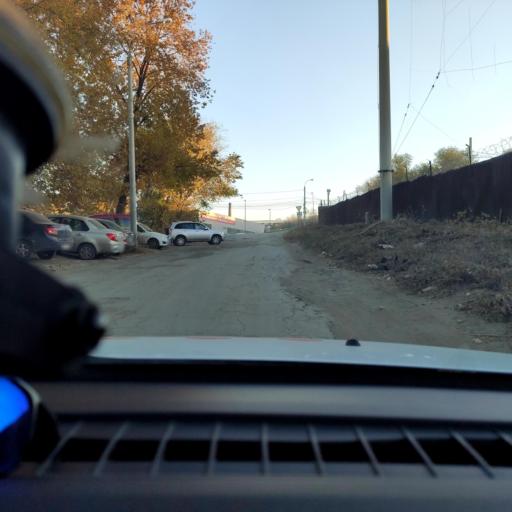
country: RU
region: Samara
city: Samara
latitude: 53.1822
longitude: 50.1521
